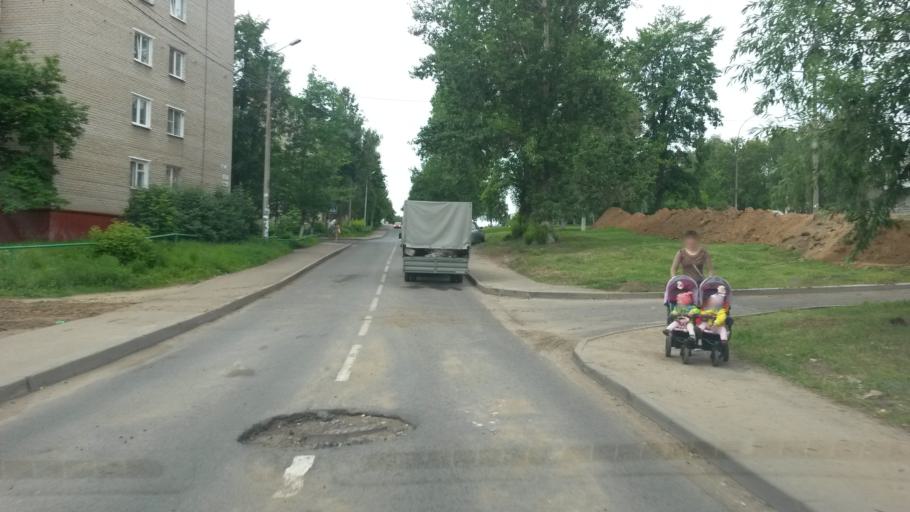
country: RU
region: Jaroslavl
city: Yaroslavl
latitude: 57.5834
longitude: 39.8634
